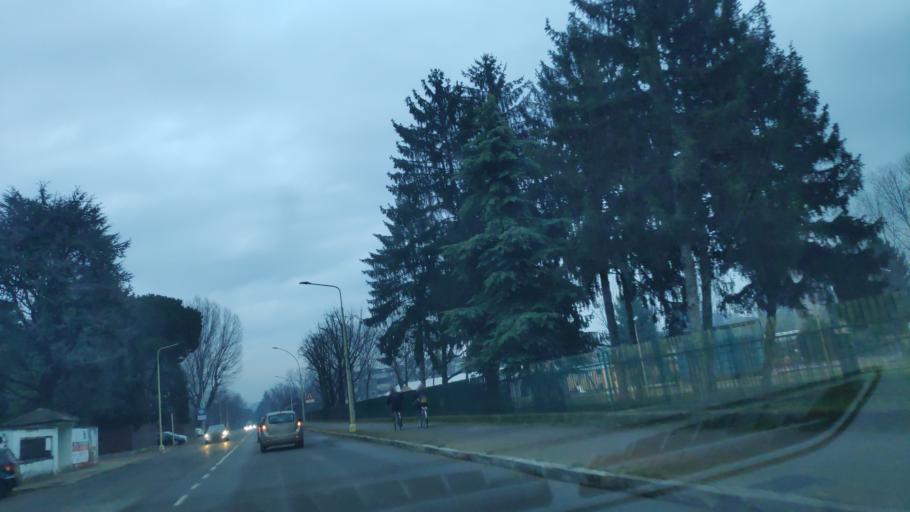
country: IT
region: Lombardy
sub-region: Citta metropolitana di Milano
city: Corsico
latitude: 45.4220
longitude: 9.1210
